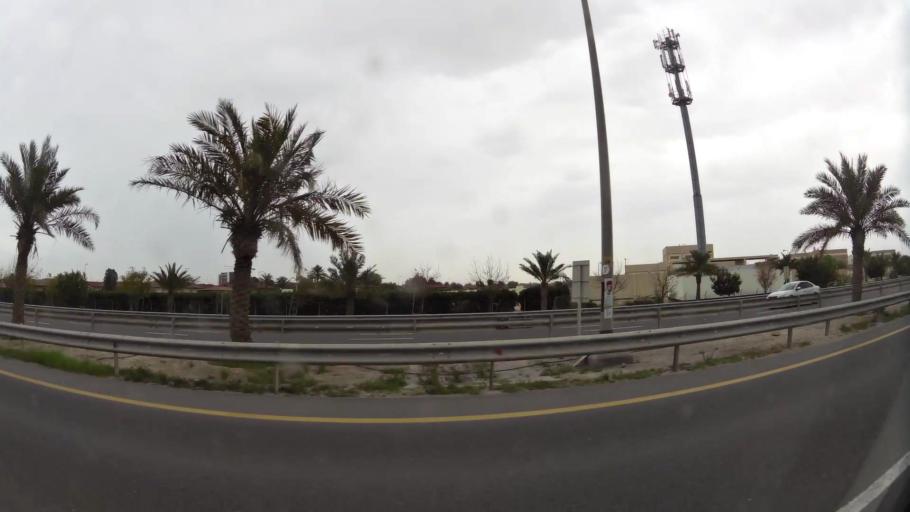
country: BH
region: Northern
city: Ar Rifa'
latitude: 26.0945
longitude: 50.5403
